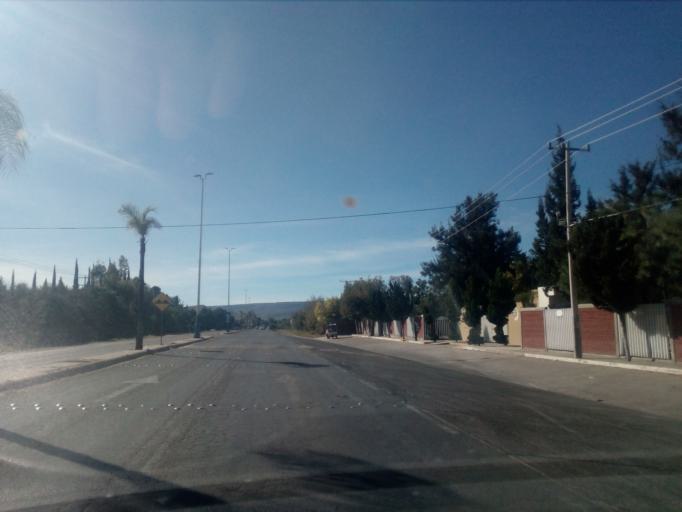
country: MX
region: Durango
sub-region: Durango
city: Sebastian Lerdo de Tejada
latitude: 23.9809
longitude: -104.6643
